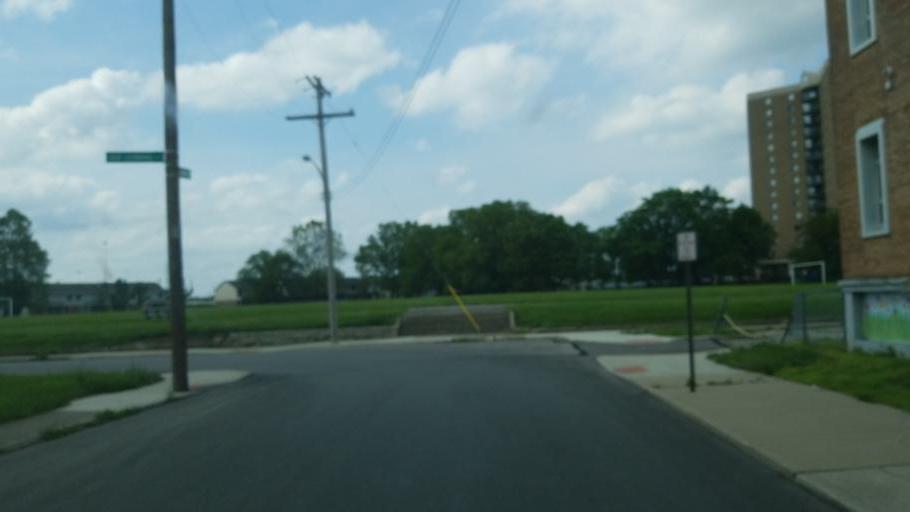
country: US
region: Ohio
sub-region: Franklin County
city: Columbus
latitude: 39.9749
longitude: -82.9780
